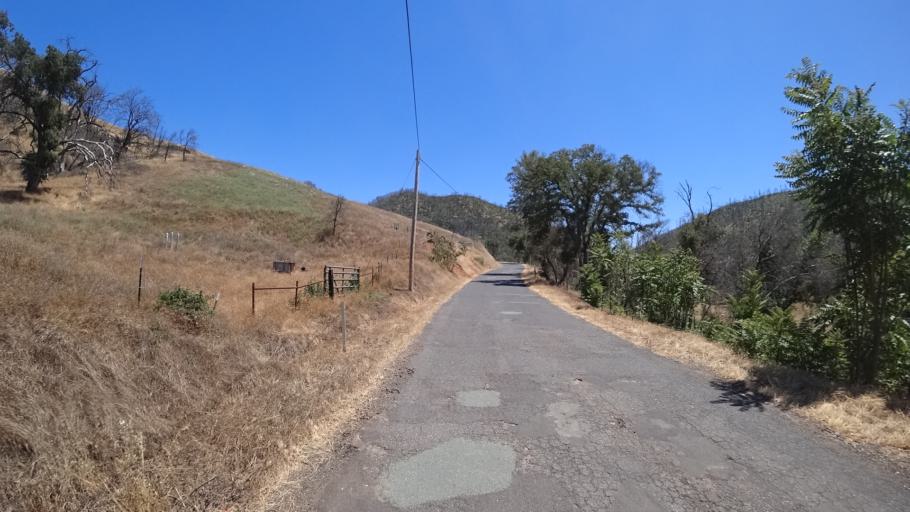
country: US
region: California
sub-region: Calaveras County
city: San Andreas
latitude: 38.2848
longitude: -120.6431
